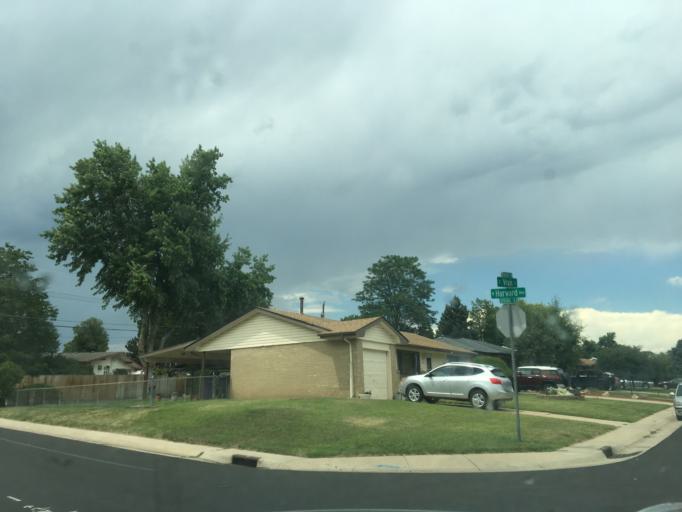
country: US
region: Colorado
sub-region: Arapahoe County
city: Sheridan
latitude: 39.6739
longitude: -105.0459
